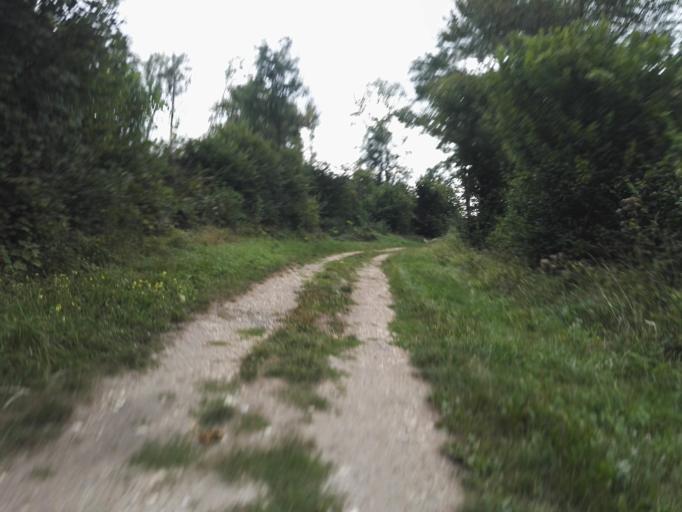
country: FR
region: Haute-Normandie
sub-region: Departement de l'Eure
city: Houlbec-Cocherel
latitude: 49.0650
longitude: 1.3068
